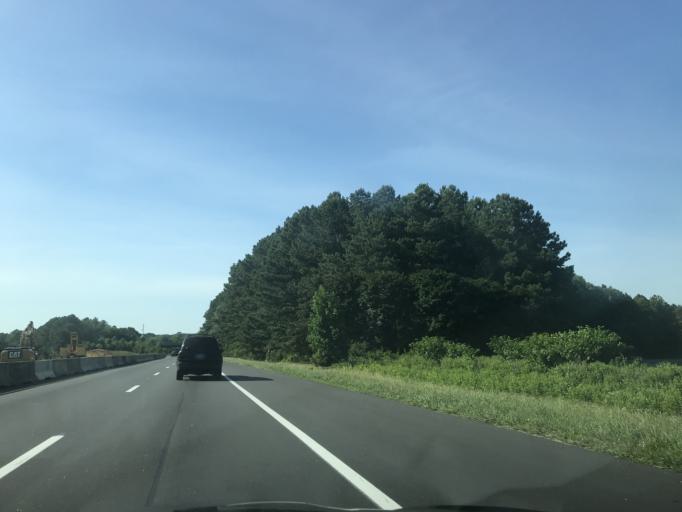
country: US
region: North Carolina
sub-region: Wake County
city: Garner
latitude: 35.7501
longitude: -78.5945
